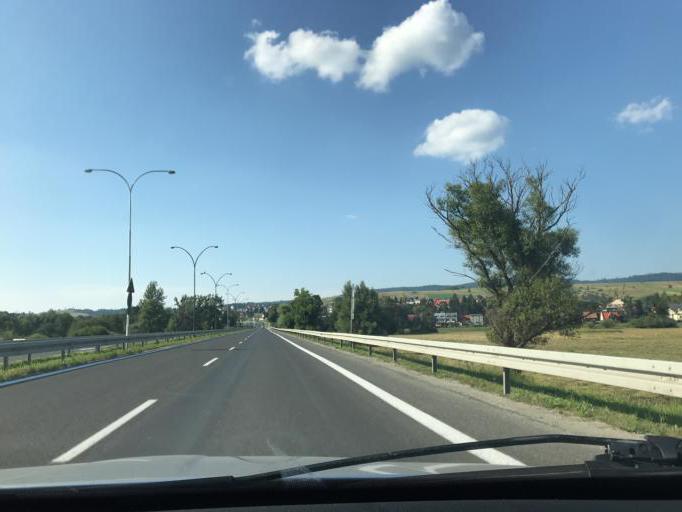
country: PL
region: Lesser Poland Voivodeship
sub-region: Powiat nowotarski
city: Nowy Targ
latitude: 49.4828
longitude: 20.0206
